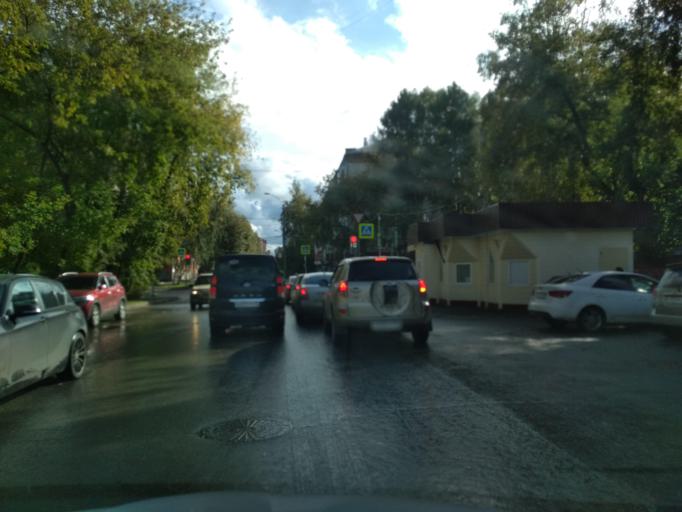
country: RU
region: Tomsk
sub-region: Tomskiy Rayon
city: Tomsk
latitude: 56.4643
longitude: 84.9756
